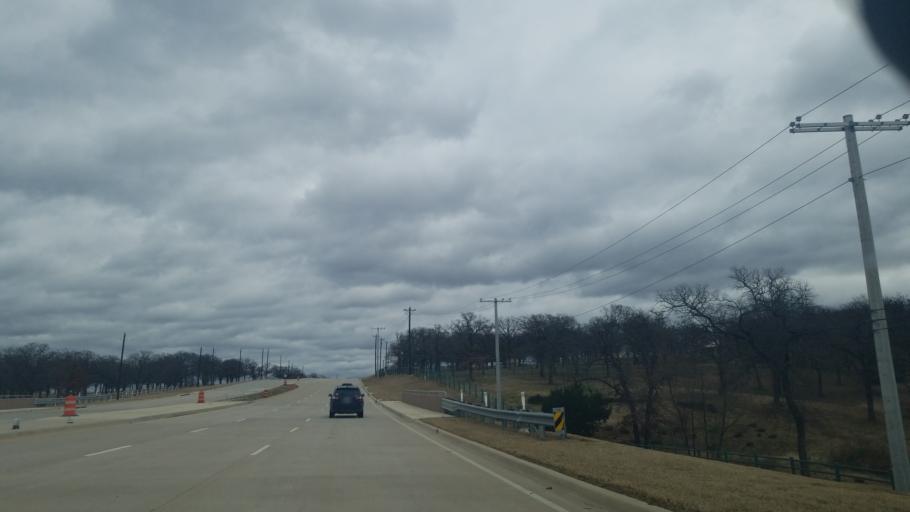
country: US
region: Texas
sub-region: Denton County
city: Bartonville
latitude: 33.0480
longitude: -97.1456
